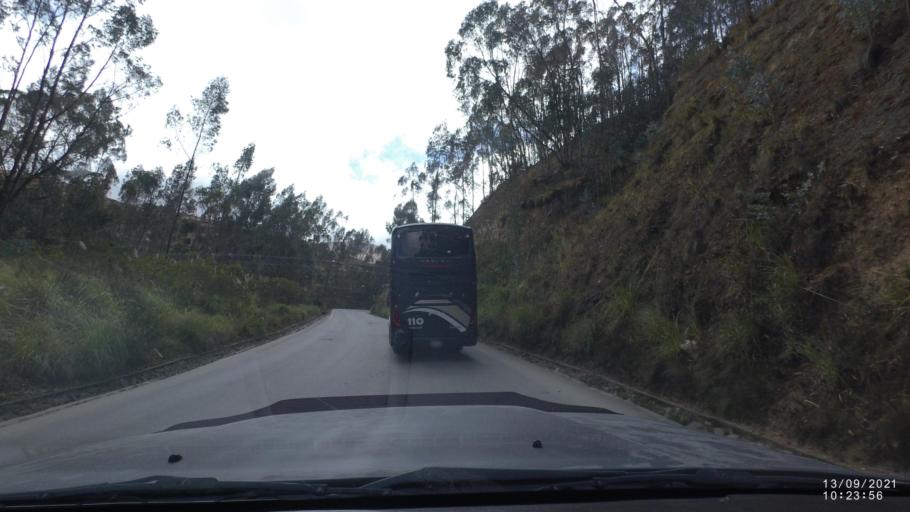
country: BO
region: Cochabamba
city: Colomi
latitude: -17.3175
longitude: -65.8643
